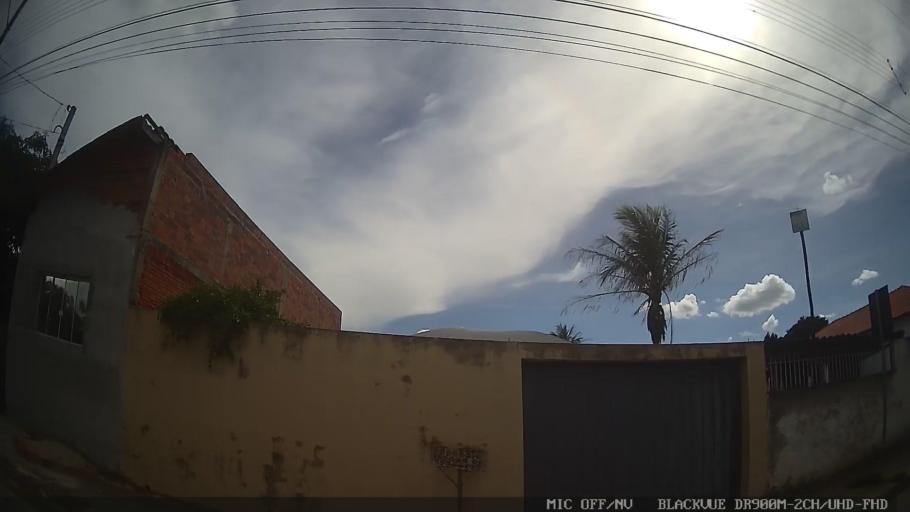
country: BR
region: Sao Paulo
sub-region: Conchas
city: Conchas
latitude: -23.0154
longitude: -48.0027
